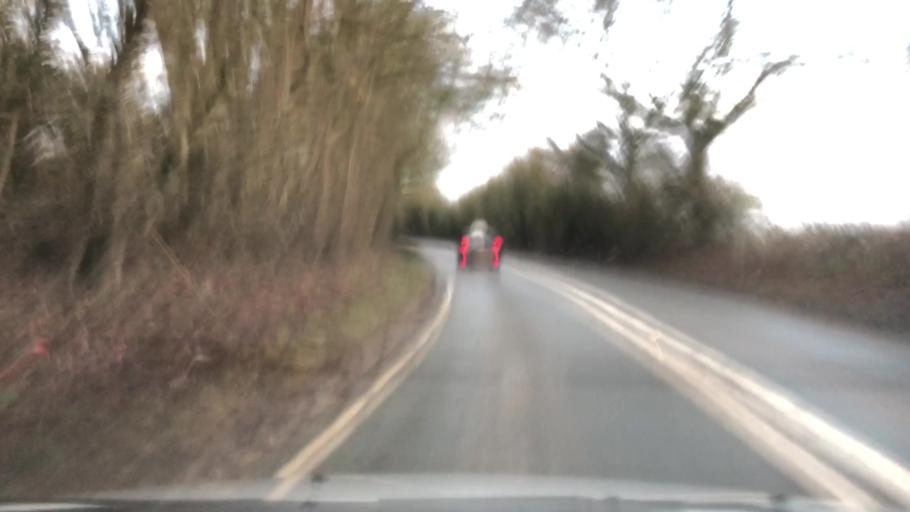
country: GB
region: England
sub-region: Hampshire
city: Alton
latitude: 51.1875
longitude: -0.9882
